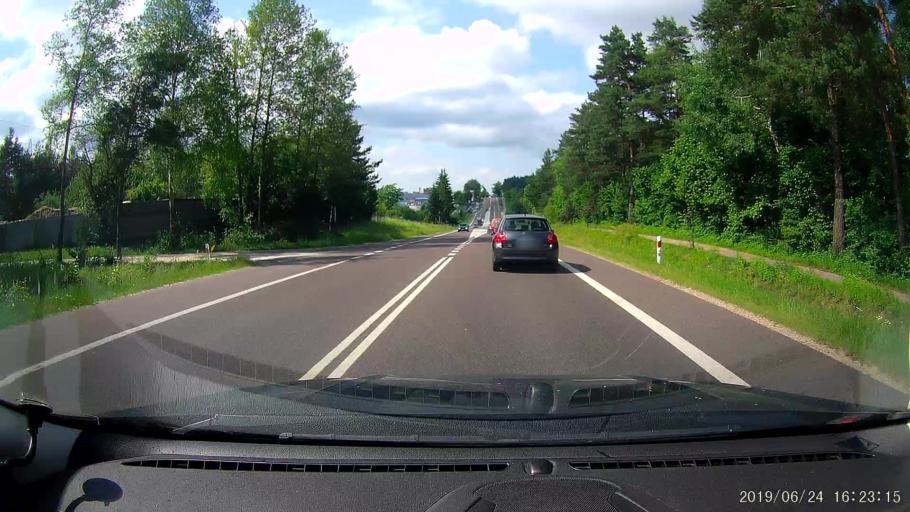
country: PL
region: Lublin Voivodeship
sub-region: Powiat tomaszowski
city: Tomaszow Lubelski
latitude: 50.4296
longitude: 23.4222
